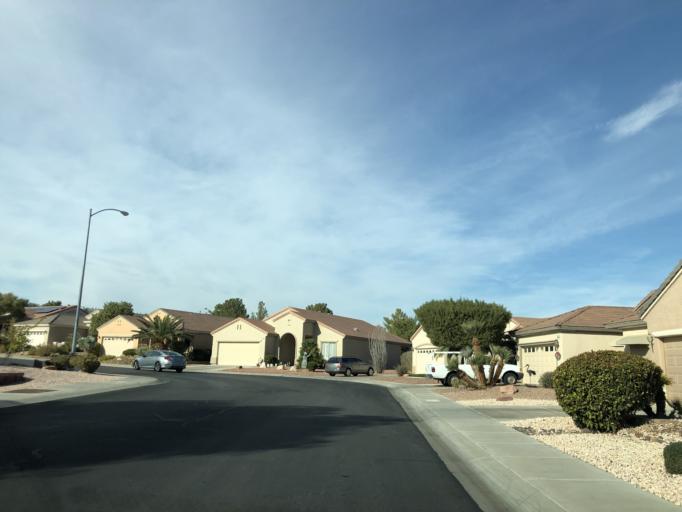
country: US
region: Nevada
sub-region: Clark County
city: Whitney
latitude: 36.0037
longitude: -115.0746
